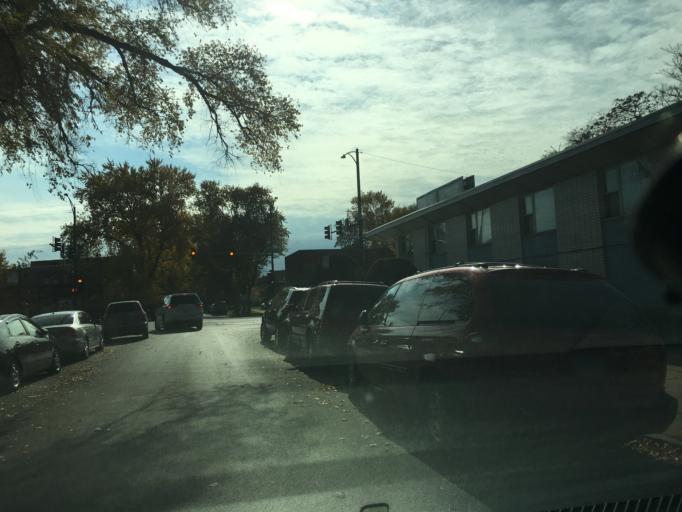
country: US
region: Illinois
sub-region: Cook County
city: Lincolnwood
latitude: 41.9910
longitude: -87.6945
